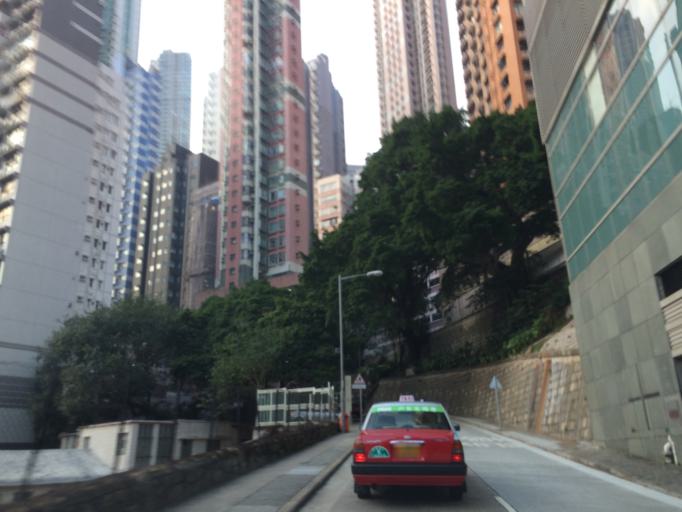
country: HK
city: Hong Kong
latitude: 22.2851
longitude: 114.1462
